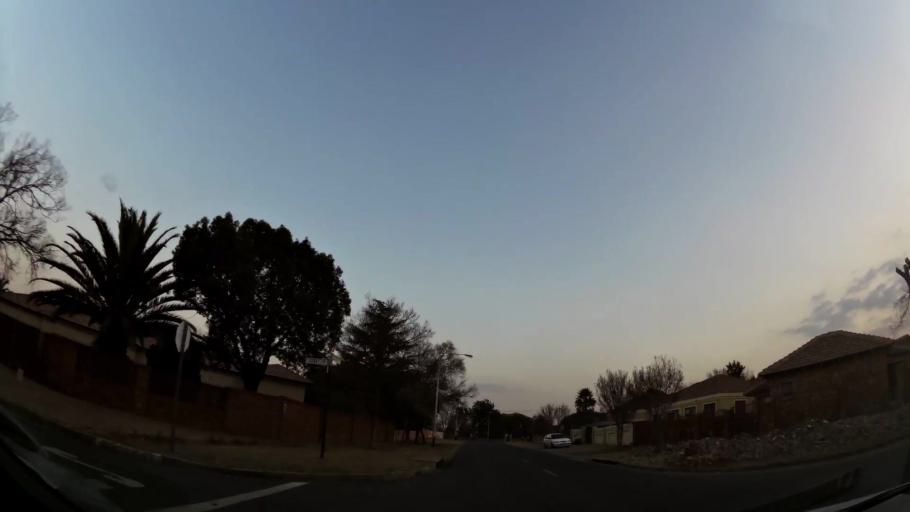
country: ZA
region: Gauteng
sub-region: Ekurhuleni Metropolitan Municipality
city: Nigel
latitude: -26.3526
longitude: 28.4390
